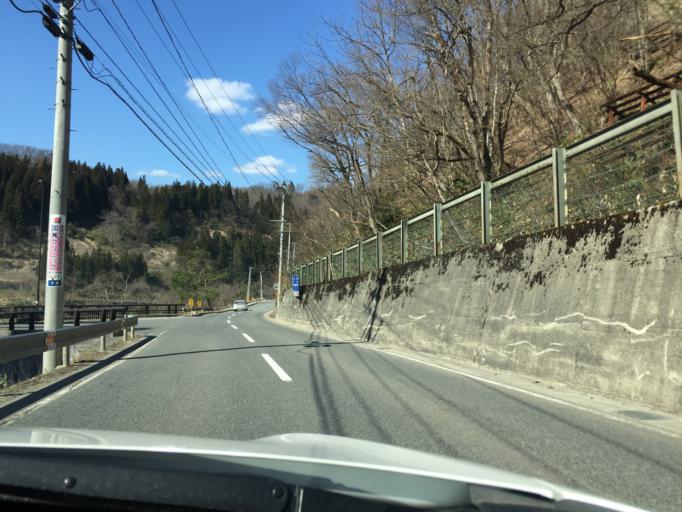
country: JP
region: Yamagata
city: Nagai
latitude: 38.2436
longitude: 140.0951
